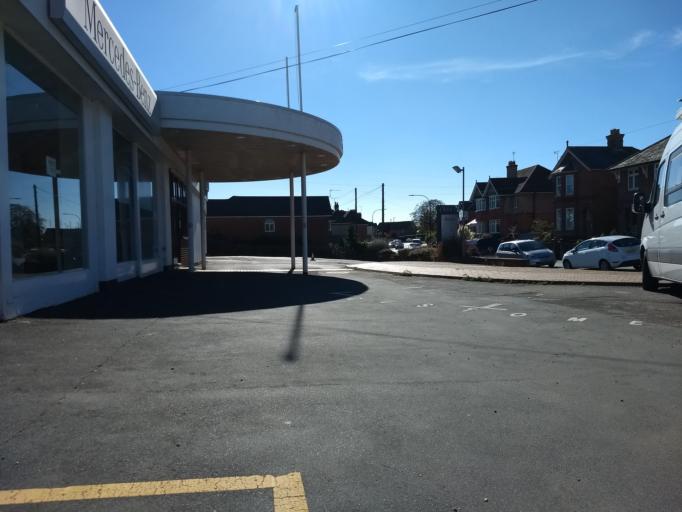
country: GB
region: England
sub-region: Isle of Wight
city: Newport
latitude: 50.6929
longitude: -1.2892
